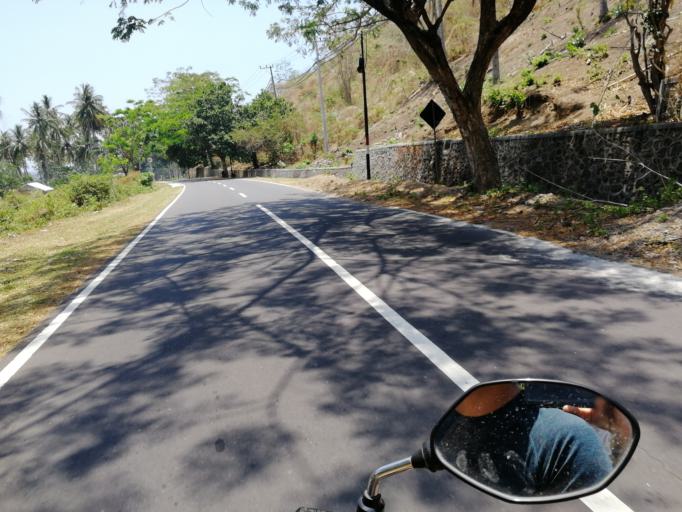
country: ID
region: West Nusa Tenggara
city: Karangsubagan
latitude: -8.4403
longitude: 116.0432
